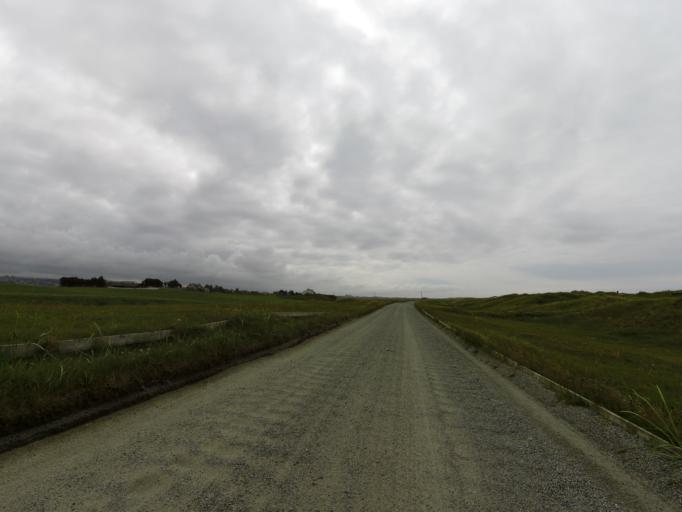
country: NO
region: Rogaland
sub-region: Klepp
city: Kleppe
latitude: 58.8066
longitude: 5.5512
